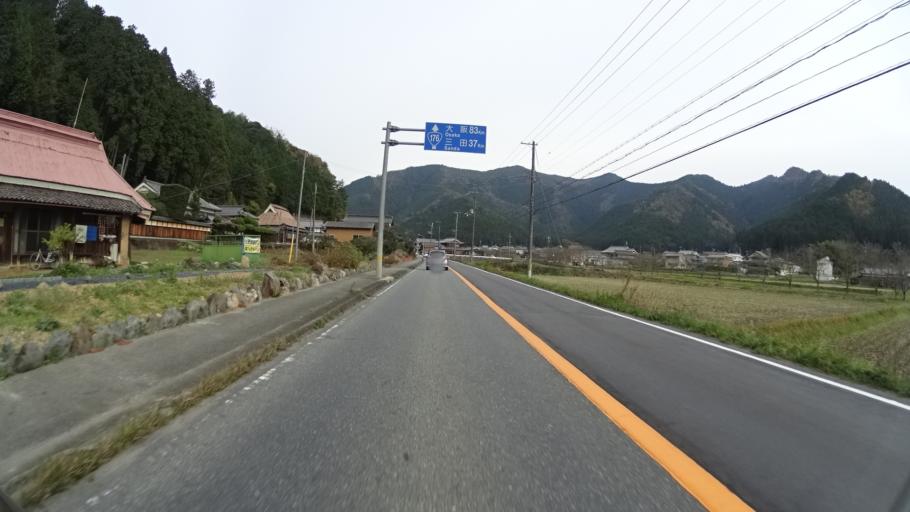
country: JP
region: Hyogo
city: Sasayama
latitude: 35.1175
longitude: 135.0918
